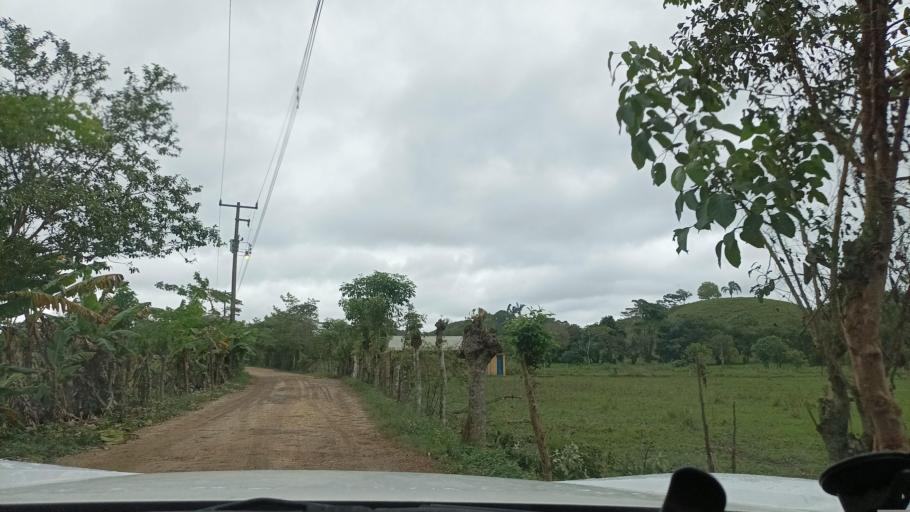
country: MX
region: Veracruz
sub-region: Moloacan
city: Cuichapa
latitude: 17.7849
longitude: -94.3878
